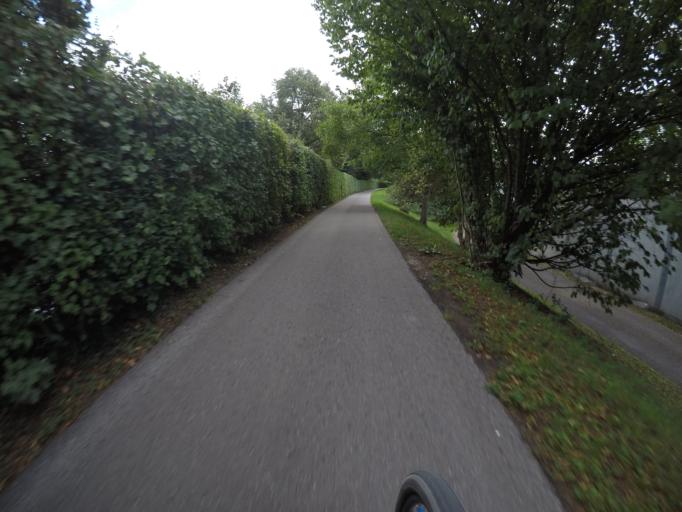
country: DE
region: Baden-Wuerttemberg
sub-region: Regierungsbezirk Stuttgart
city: Stuttgart Muehlhausen
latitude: 48.8395
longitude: 9.2284
